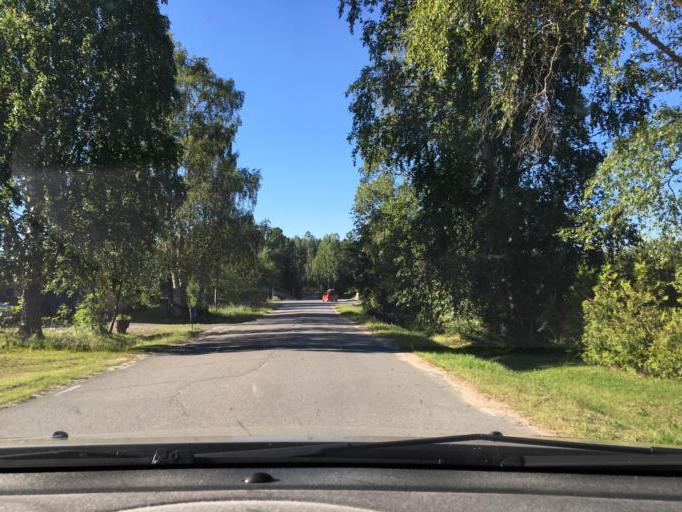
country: SE
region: Norrbotten
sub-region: Kalix Kommun
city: Toere
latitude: 66.0686
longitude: 22.7014
